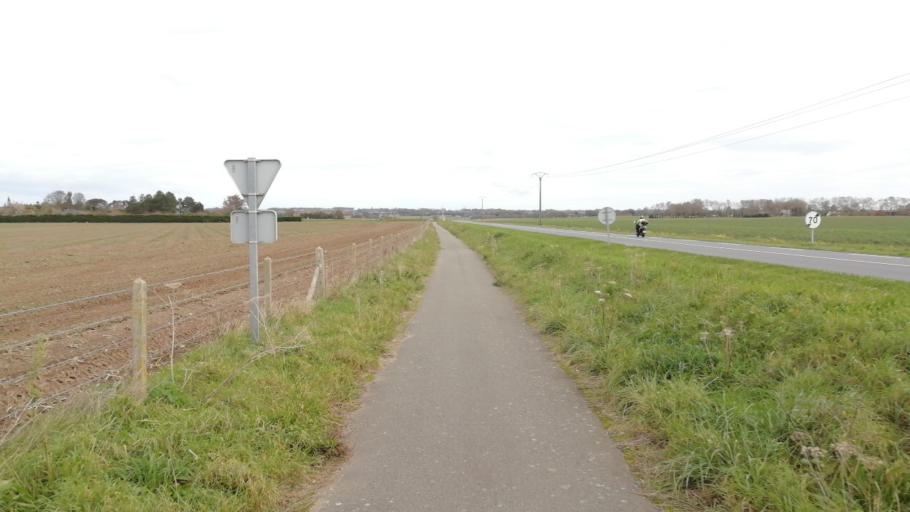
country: FR
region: Haute-Normandie
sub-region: Departement de la Seine-Maritime
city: Cauville-sur-Mer
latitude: 49.5958
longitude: 0.1359
